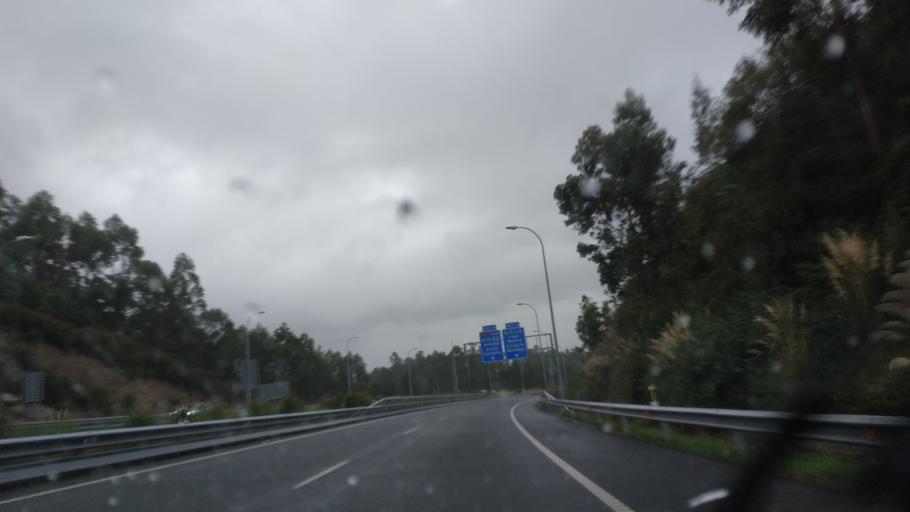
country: ES
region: Galicia
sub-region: Provincia da Coruna
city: Culleredo
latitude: 43.2820
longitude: -8.3942
